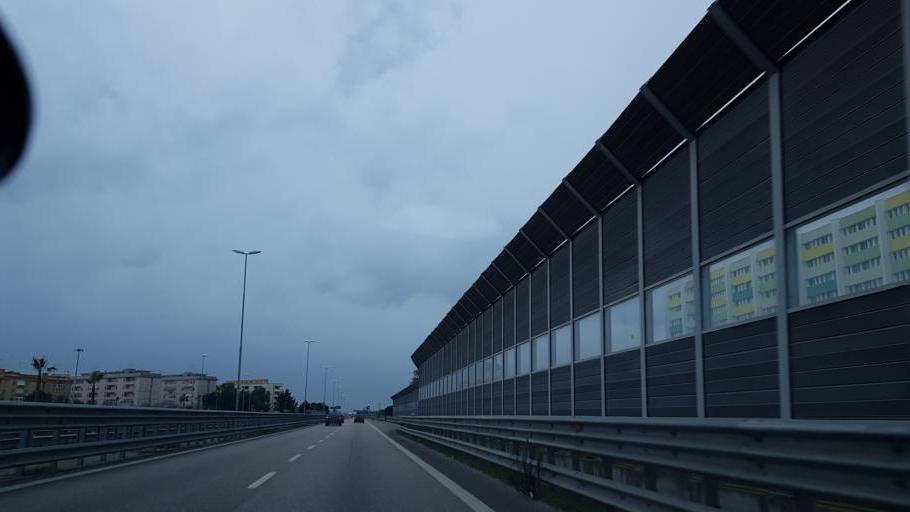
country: IT
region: Apulia
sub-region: Provincia di Brindisi
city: Brindisi
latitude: 40.6238
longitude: 17.9156
